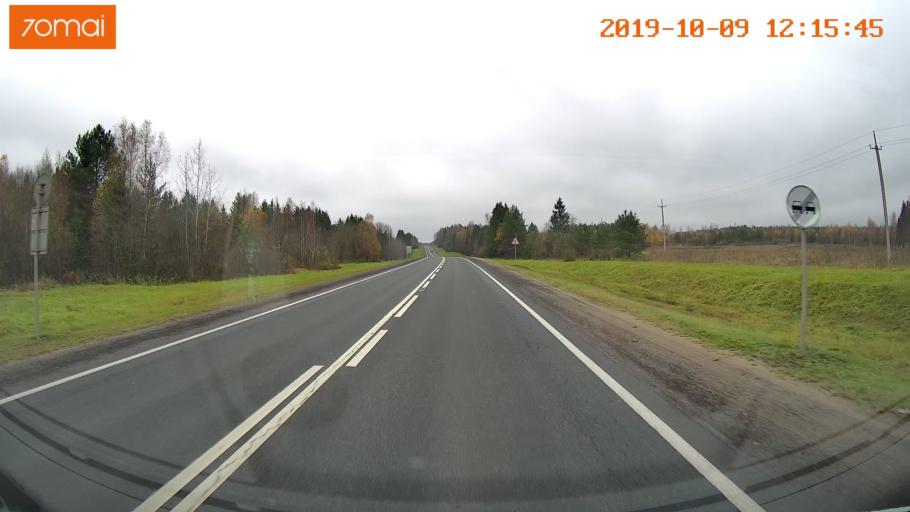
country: RU
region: Jaroslavl
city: Prechistoye
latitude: 58.4788
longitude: 40.3226
